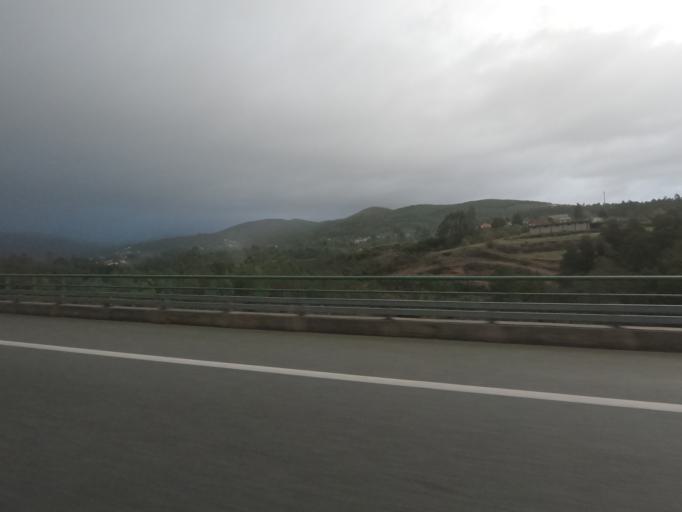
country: PT
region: Viana do Castelo
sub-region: Ponte de Lima
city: Ponte de Lima
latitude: 41.8127
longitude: -8.5992
